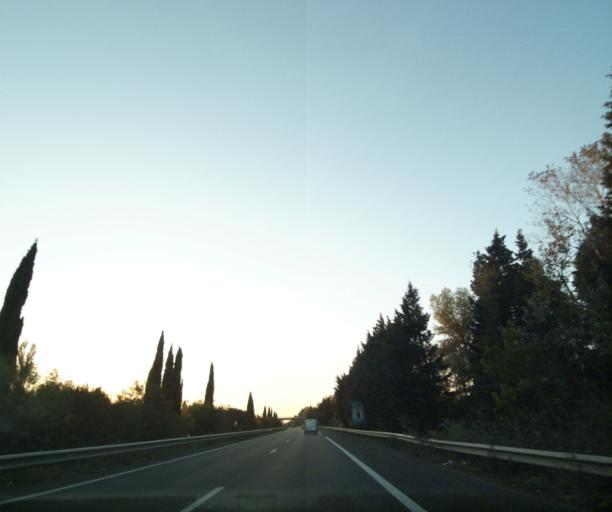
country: FR
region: Provence-Alpes-Cote d'Azur
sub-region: Departement des Bouches-du-Rhone
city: Saint-Martin-de-Crau
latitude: 43.6383
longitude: 4.8498
